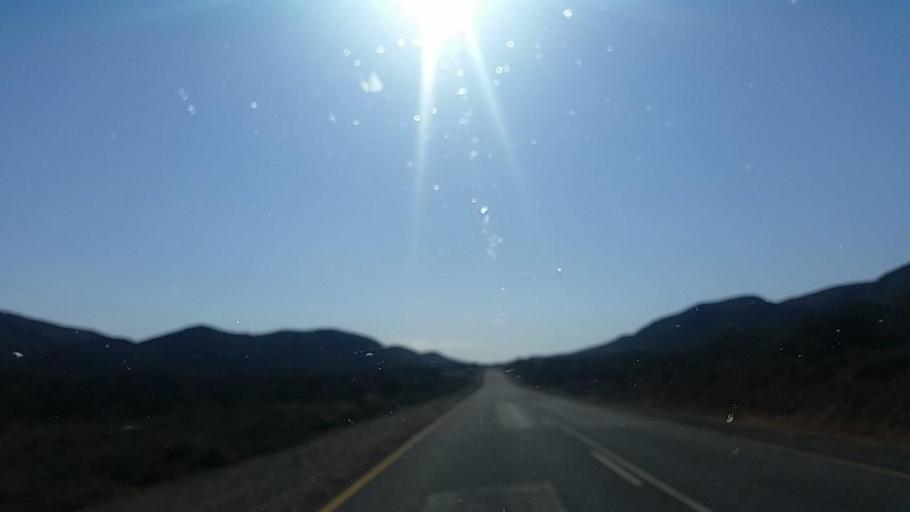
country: ZA
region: Eastern Cape
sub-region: Cacadu District Municipality
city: Willowmore
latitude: -33.4105
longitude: 23.3236
